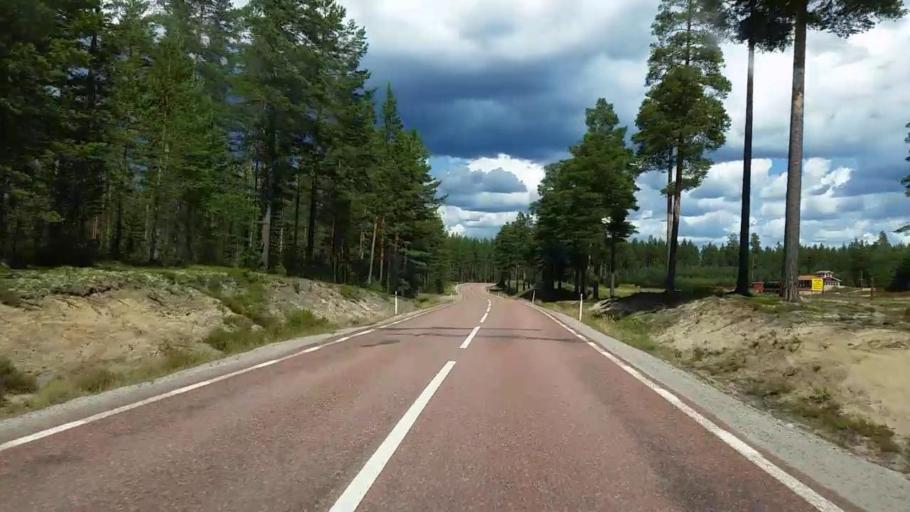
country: SE
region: Gaevleborg
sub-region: Ovanakers Kommun
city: Edsbyn
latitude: 61.3472
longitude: 15.5718
